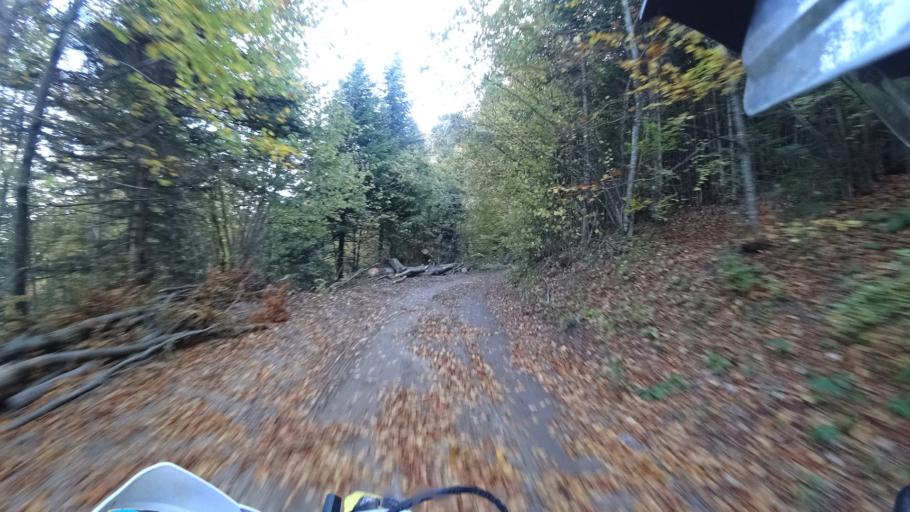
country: HR
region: Karlovacka
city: Plaski
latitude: 45.0329
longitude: 15.3788
